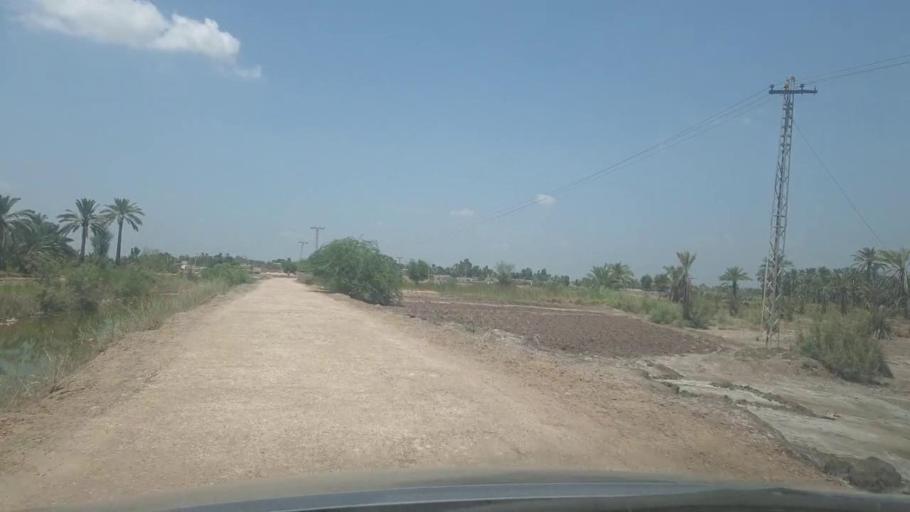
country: PK
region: Sindh
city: Kot Diji
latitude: 27.4165
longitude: 68.7363
